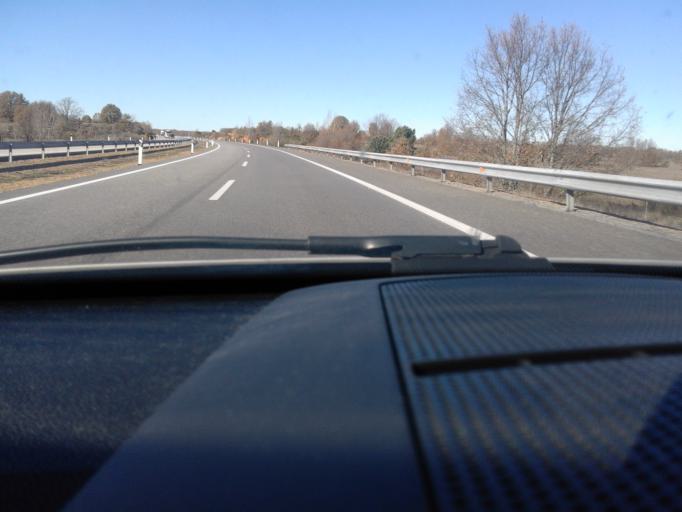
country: ES
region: Castille and Leon
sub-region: Provincia de Leon
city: Valverde de la Virgen
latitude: 42.6037
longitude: -5.7131
